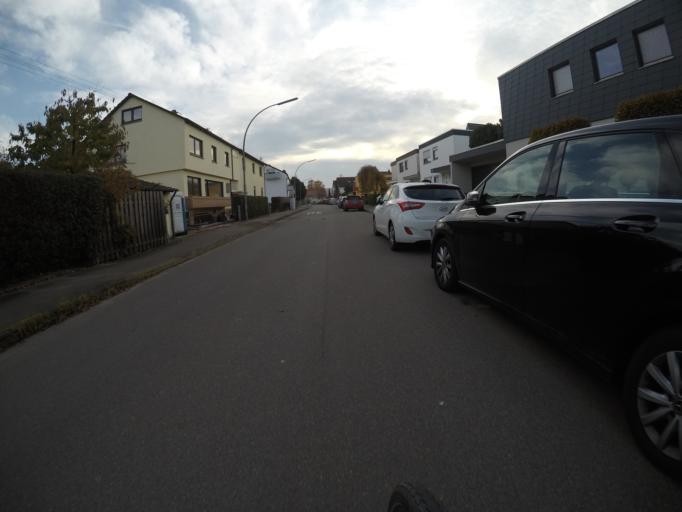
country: DE
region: Baden-Wuerttemberg
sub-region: Regierungsbezirk Stuttgart
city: Leinfelden-Echterdingen
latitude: 48.6859
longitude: 9.1611
